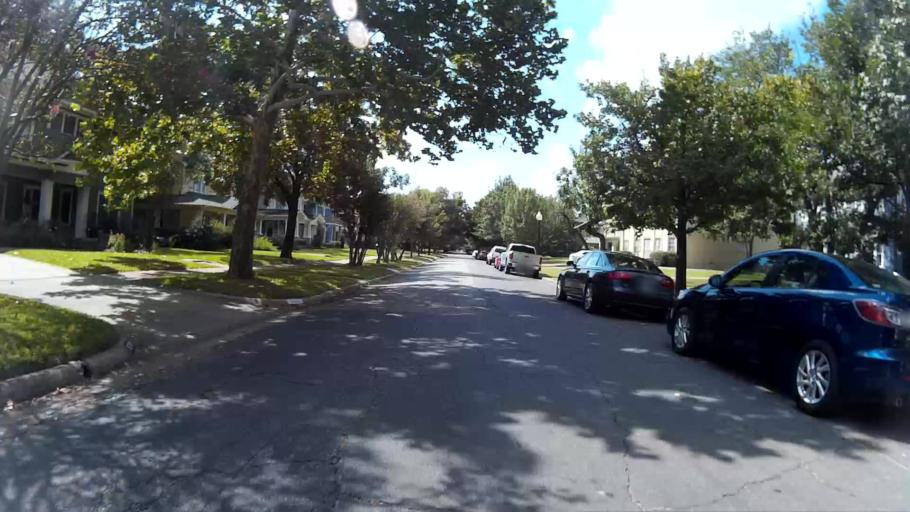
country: US
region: Texas
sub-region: Dallas County
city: Highland Park
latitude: 32.8016
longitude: -96.7655
